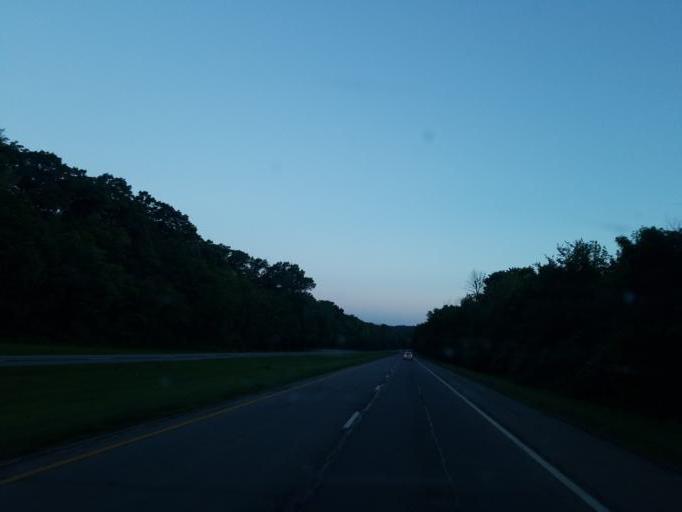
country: US
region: Ohio
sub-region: Summit County
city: Clinton
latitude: 40.8987
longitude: -81.6384
